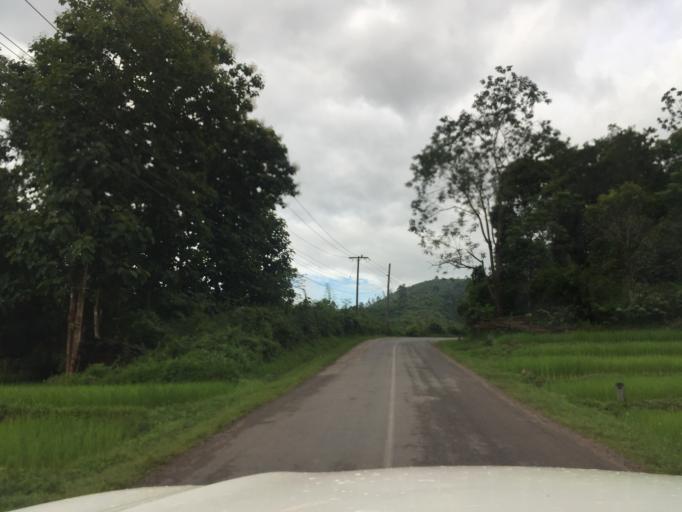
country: LA
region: Oudomxai
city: Muang La
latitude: 20.7888
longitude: 102.0794
